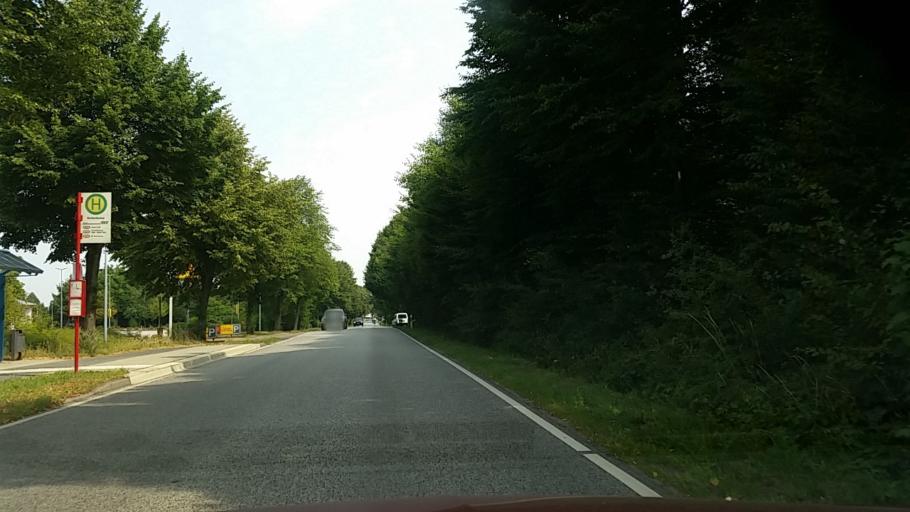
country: DE
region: Schleswig-Holstein
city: Schmilau
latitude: 53.6883
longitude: 10.7491
